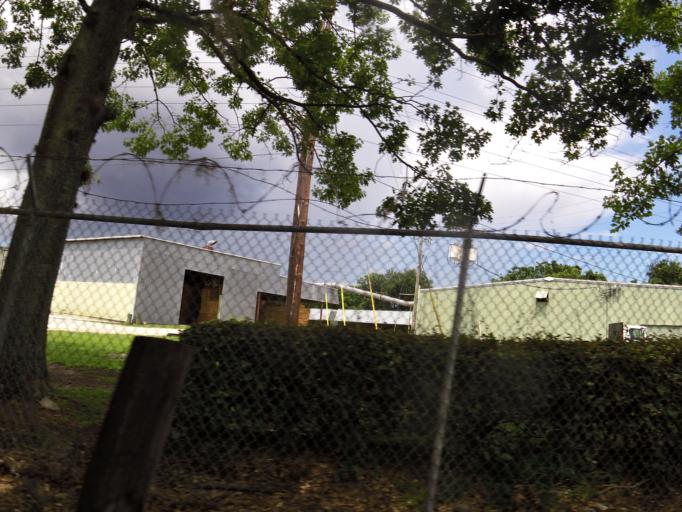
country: US
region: Florida
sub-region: Duval County
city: Jacksonville
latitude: 30.3687
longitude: -81.6386
